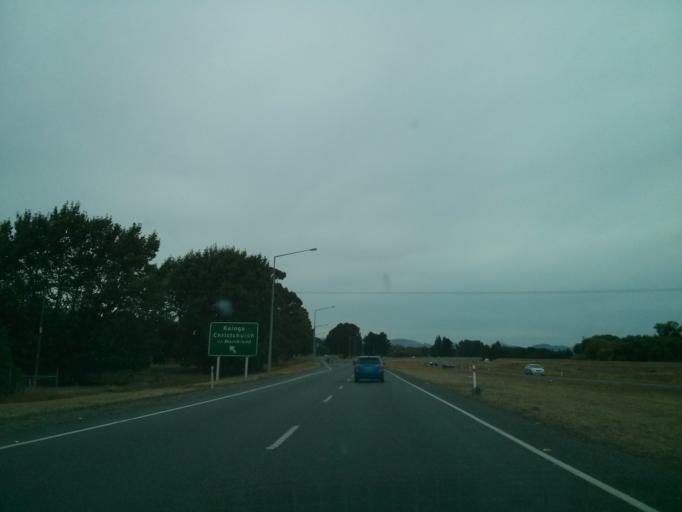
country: NZ
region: Canterbury
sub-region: Waimakariri District
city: Kaiapoi
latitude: -43.4193
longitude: 172.6481
